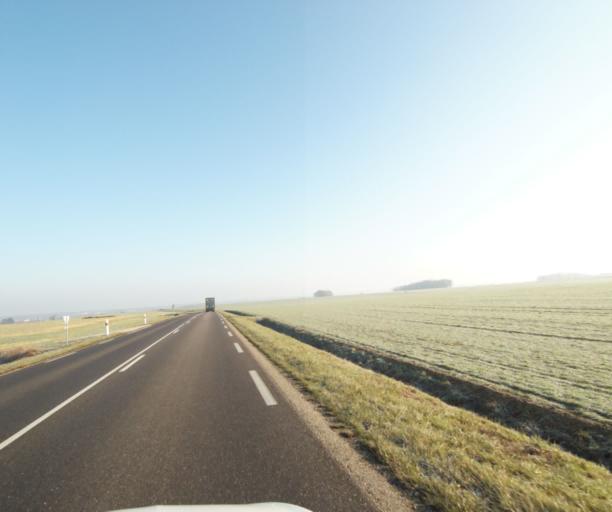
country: FR
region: Champagne-Ardenne
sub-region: Departement de la Haute-Marne
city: Montier-en-Der
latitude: 48.4541
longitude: 4.7441
